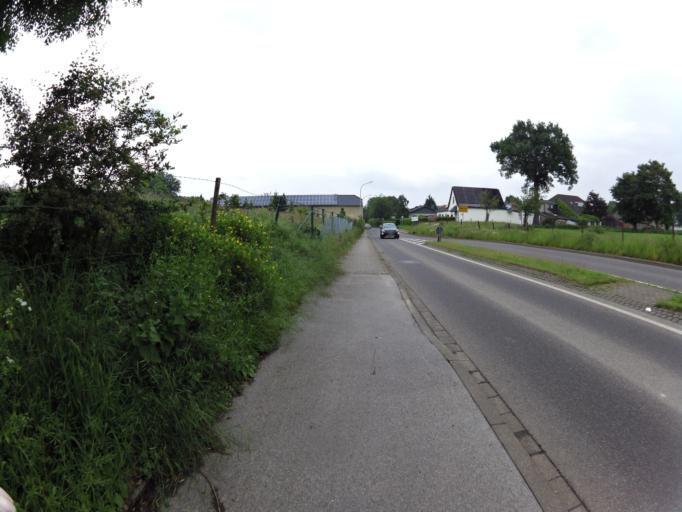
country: DE
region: North Rhine-Westphalia
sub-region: Regierungsbezirk Koln
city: Ubach-Palenberg
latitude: 50.9422
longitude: 6.1564
